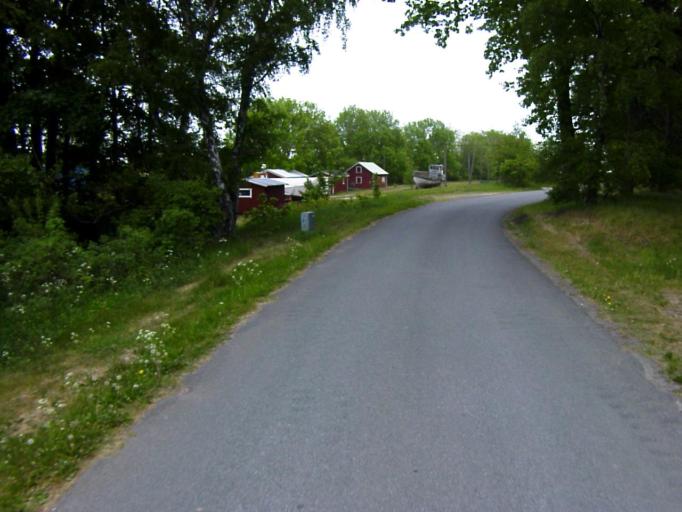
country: SE
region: Skane
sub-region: Kristianstads Kommun
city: Ahus
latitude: 55.9250
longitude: 14.3060
